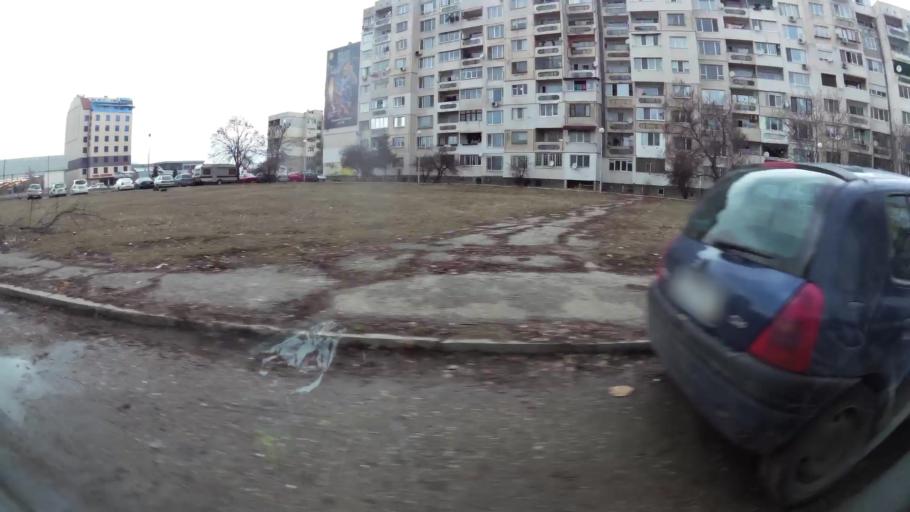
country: BG
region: Sofia-Capital
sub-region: Stolichna Obshtina
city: Sofia
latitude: 42.7322
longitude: 23.2867
